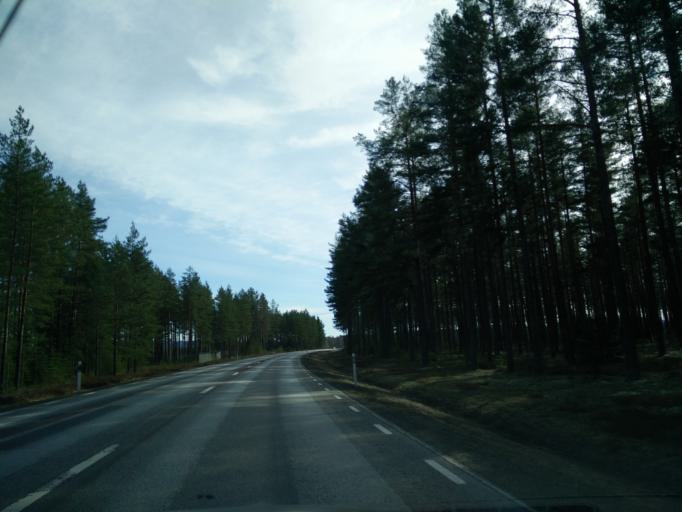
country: SE
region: Vaermland
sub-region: Hagfors Kommun
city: Hagfors
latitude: 60.0409
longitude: 13.5849
